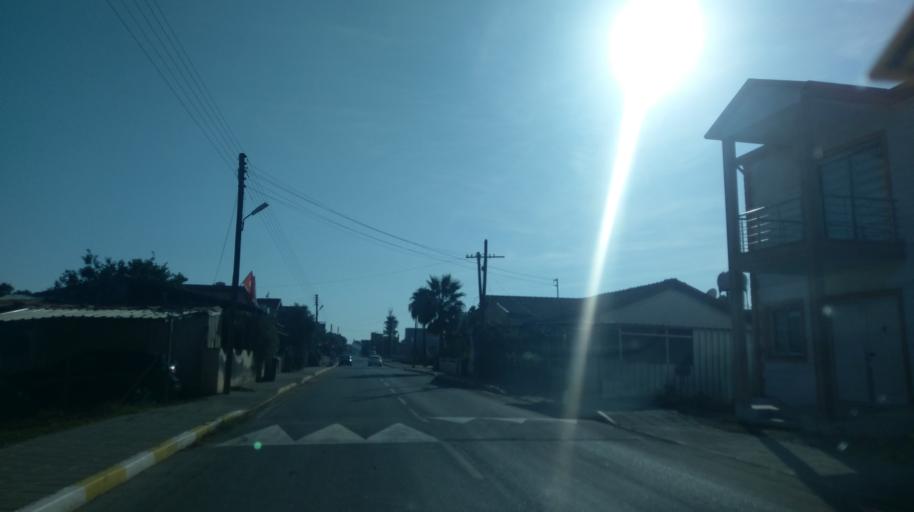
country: CY
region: Larnaka
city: Pergamos
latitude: 35.0454
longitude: 33.7089
